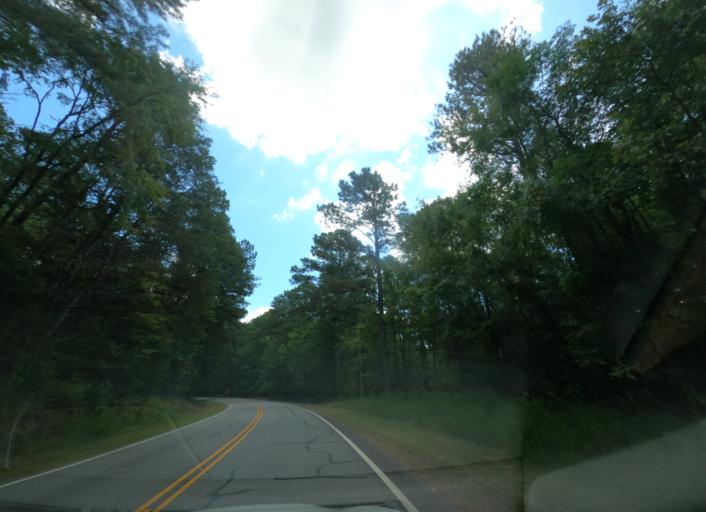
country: US
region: South Carolina
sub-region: McCormick County
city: McCormick
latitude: 33.8881
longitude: -82.3995
